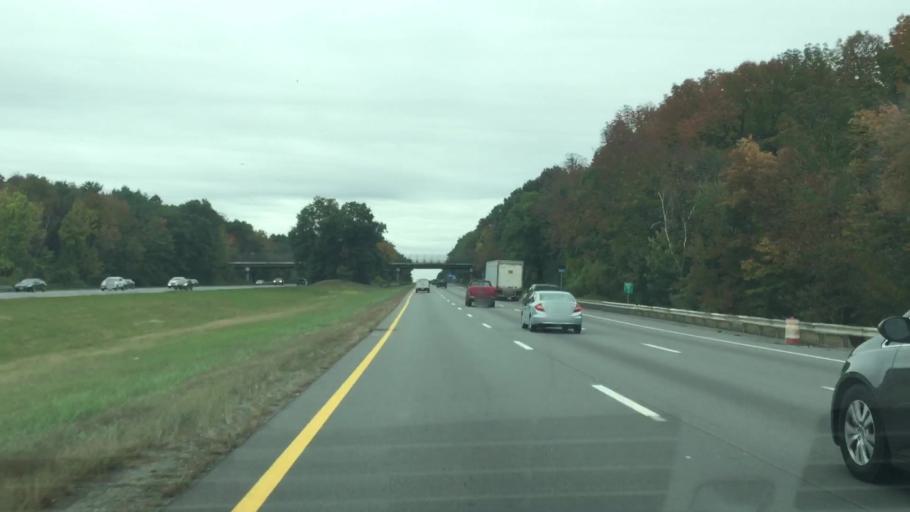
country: US
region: Massachusetts
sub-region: Essex County
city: Lawrence
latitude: 42.6607
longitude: -71.1991
